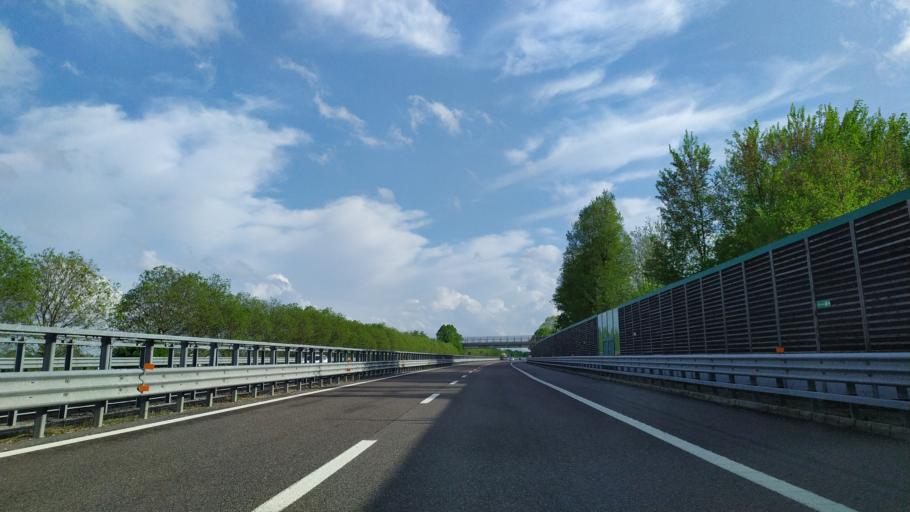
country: IT
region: Veneto
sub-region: Provincia di Vicenza
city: Vigardolo
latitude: 45.6137
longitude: 11.5996
